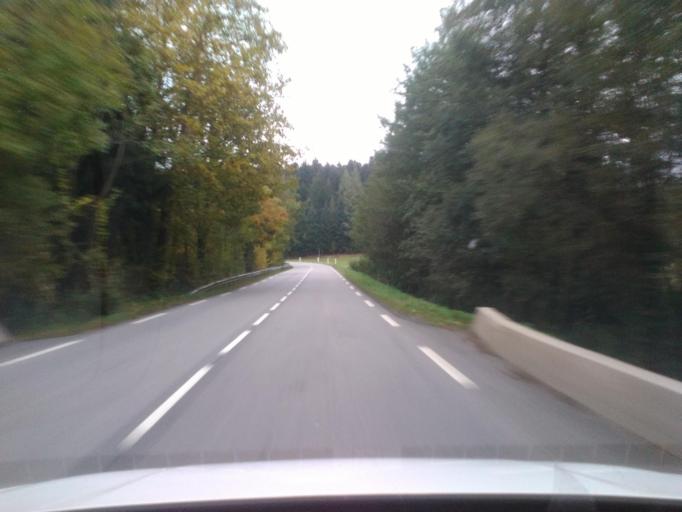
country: FR
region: Lorraine
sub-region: Departement des Vosges
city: Ban-de-Laveline
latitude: 48.3191
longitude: 7.0936
